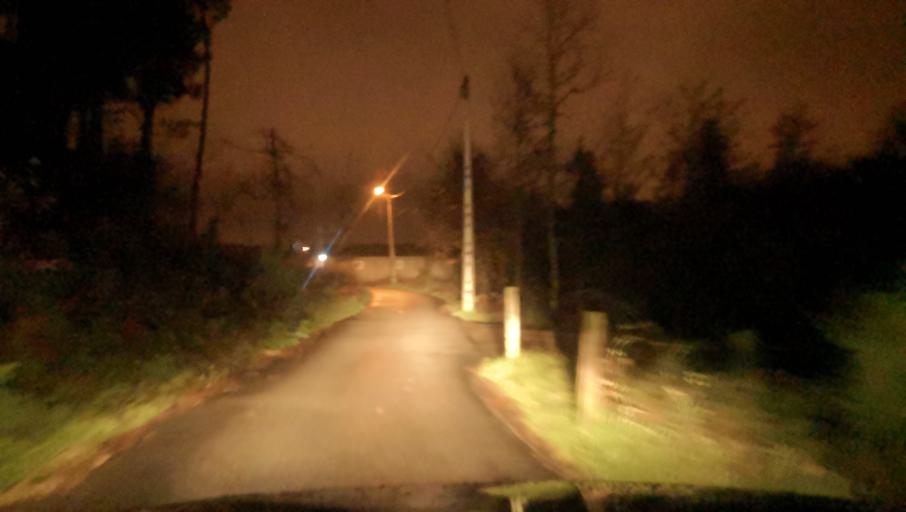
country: PT
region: Vila Real
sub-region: Vila Real
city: Vila Real
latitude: 41.3217
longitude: -7.7208
